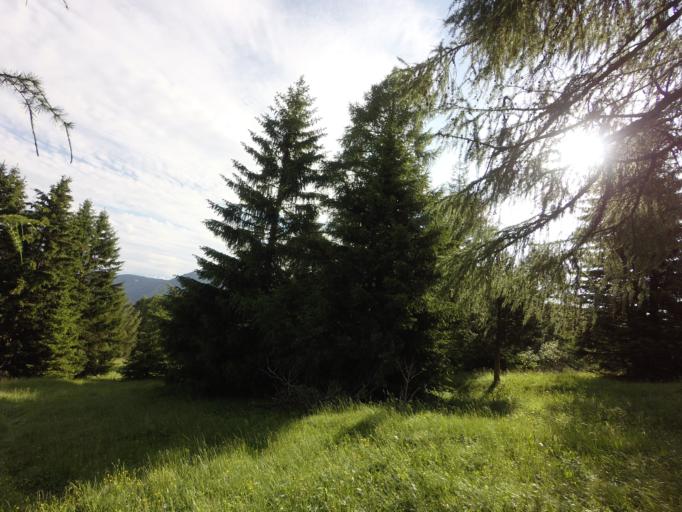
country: IT
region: Trentino-Alto Adige
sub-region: Bolzano
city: Ortisei
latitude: 46.5452
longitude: 11.6314
